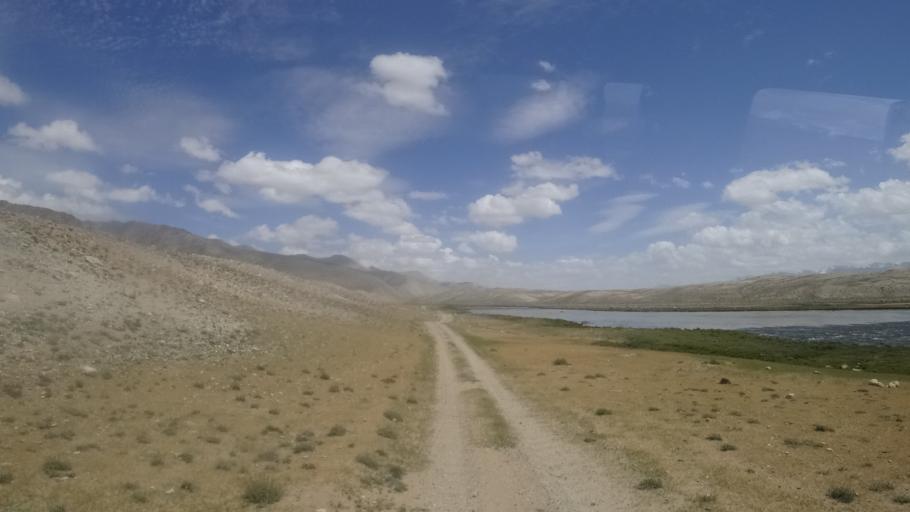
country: TJ
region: Gorno-Badakhshan
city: Murghob
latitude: 37.4680
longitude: 73.4200
